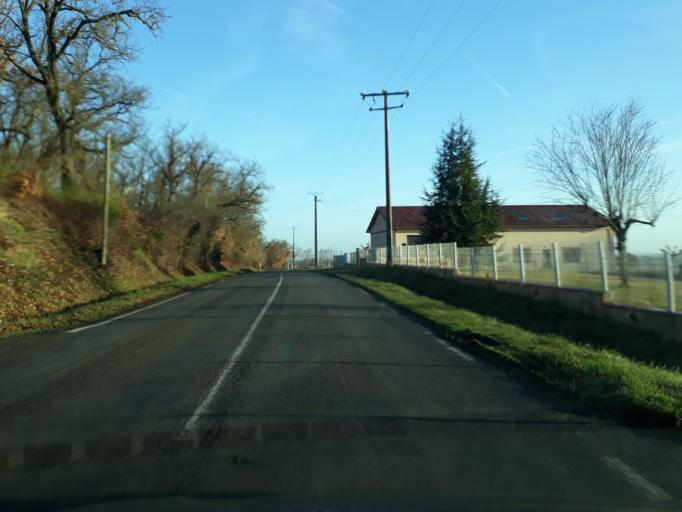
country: FR
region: Midi-Pyrenees
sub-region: Departement de la Haute-Garonne
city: Sainte-Foy-de-Peyrolieres
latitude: 43.4911
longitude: 1.1505
